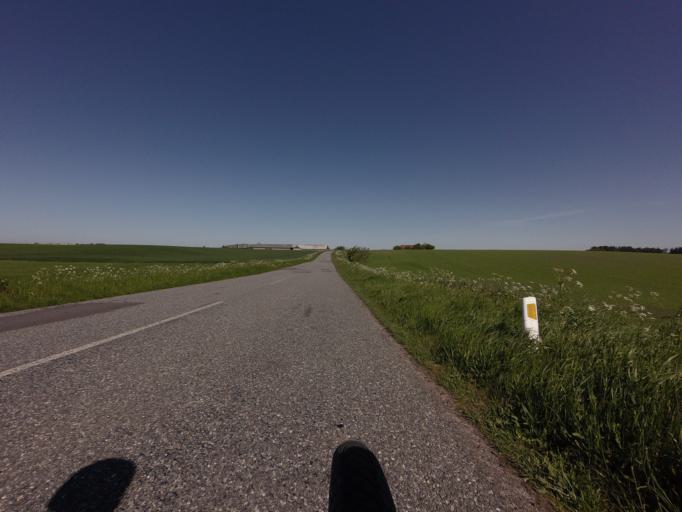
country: DK
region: North Denmark
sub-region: Hjorring Kommune
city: Hjorring
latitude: 57.4412
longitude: 9.8998
